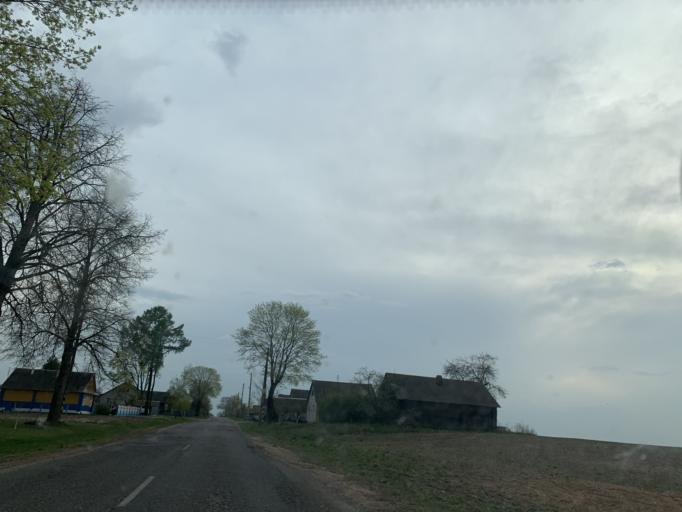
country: BY
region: Minsk
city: Kapyl'
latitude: 53.2856
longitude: 26.9846
